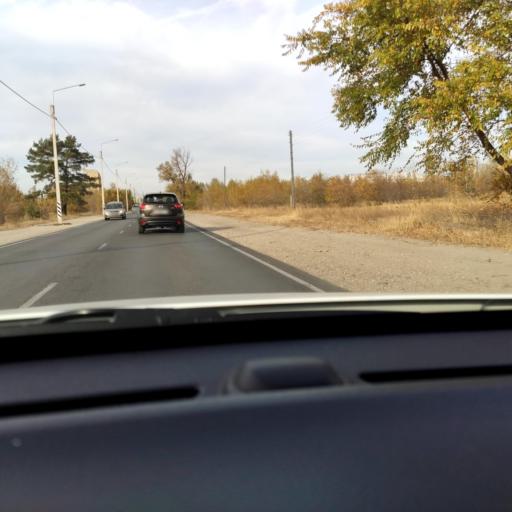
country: RU
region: Voronezj
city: Maslovka
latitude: 51.5828
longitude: 39.2476
